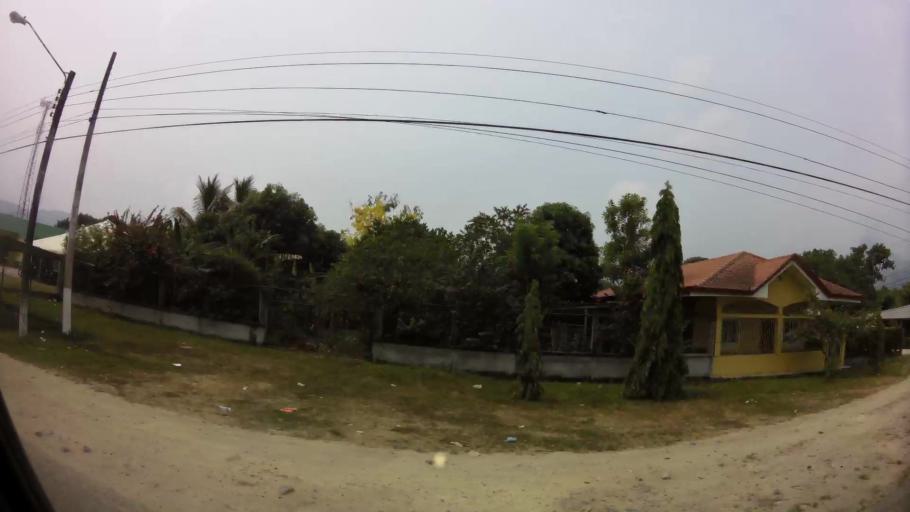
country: HN
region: Atlantida
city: San Juan Pueblo
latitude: 15.5985
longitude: -87.2150
